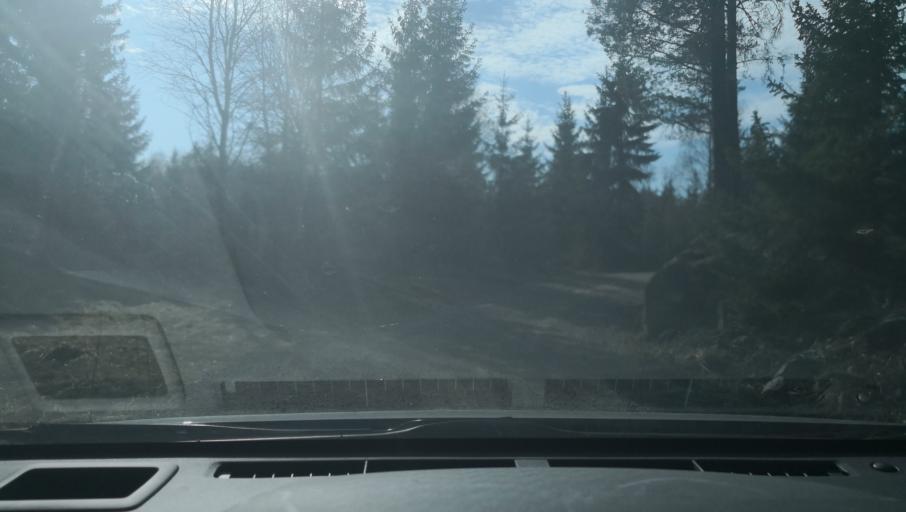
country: SE
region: Uppsala
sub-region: Heby Kommun
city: Heby
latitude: 59.8405
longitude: 16.8607
